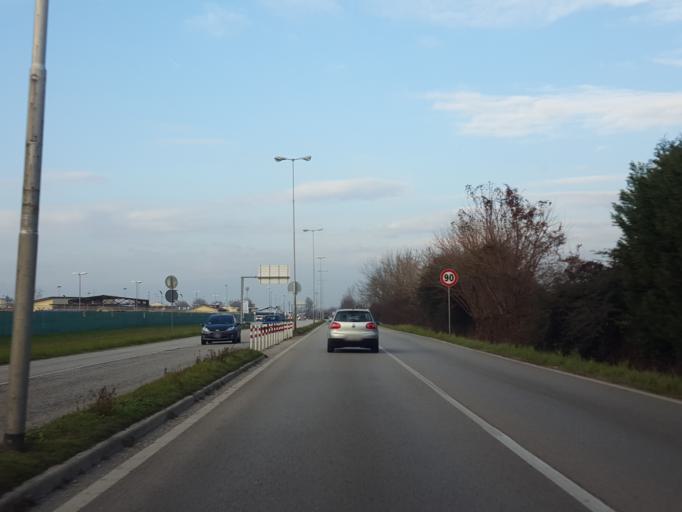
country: IT
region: Veneto
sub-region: Provincia di Vicenza
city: Villaggio Montegrappa
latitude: 45.5426
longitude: 11.5863
